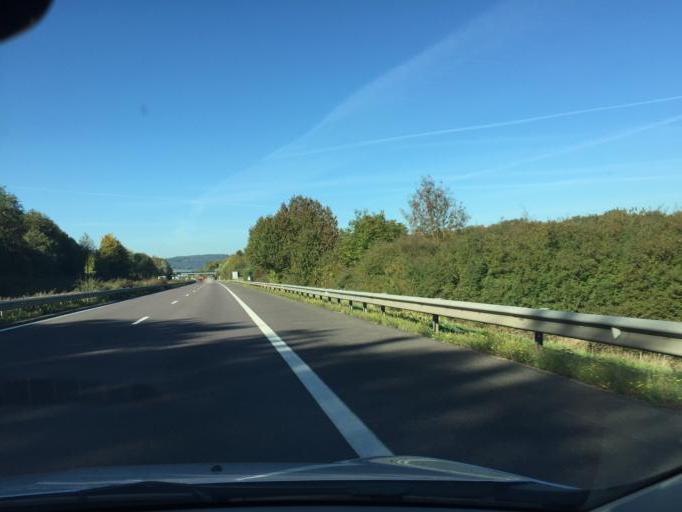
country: LU
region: Luxembourg
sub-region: Canton de Luxembourg
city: Schuttrange
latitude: 49.6433
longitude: 6.2966
